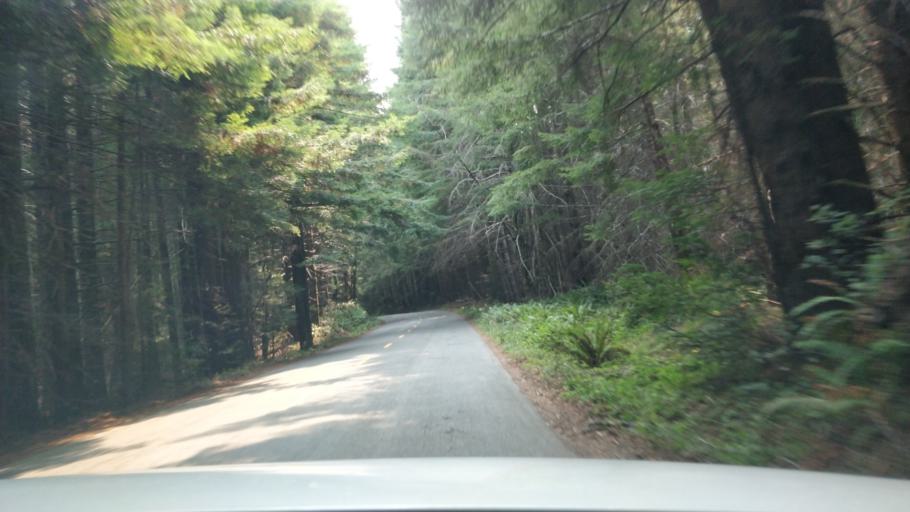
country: US
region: California
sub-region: Humboldt County
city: Westhaven-Moonstone
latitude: 41.2434
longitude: -123.9824
